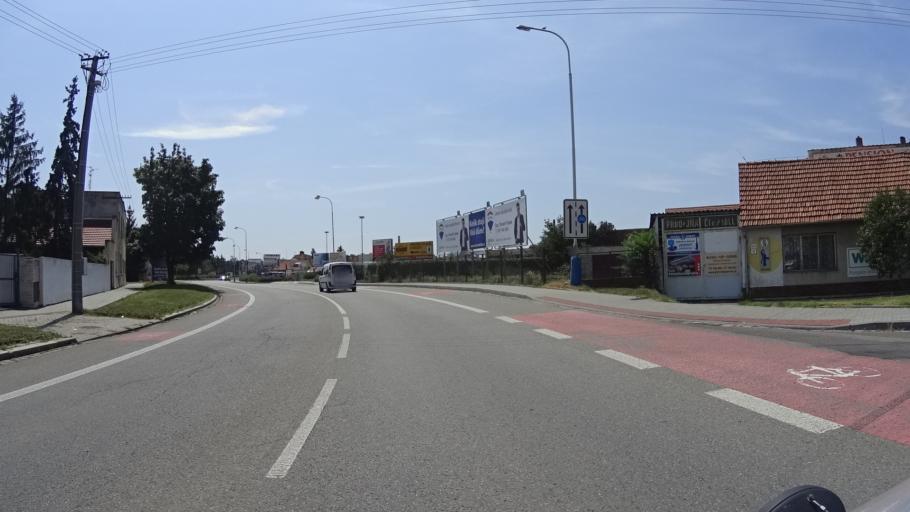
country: CZ
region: South Moravian
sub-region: Okres Breclav
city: Breclav
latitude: 48.7738
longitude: 16.8913
